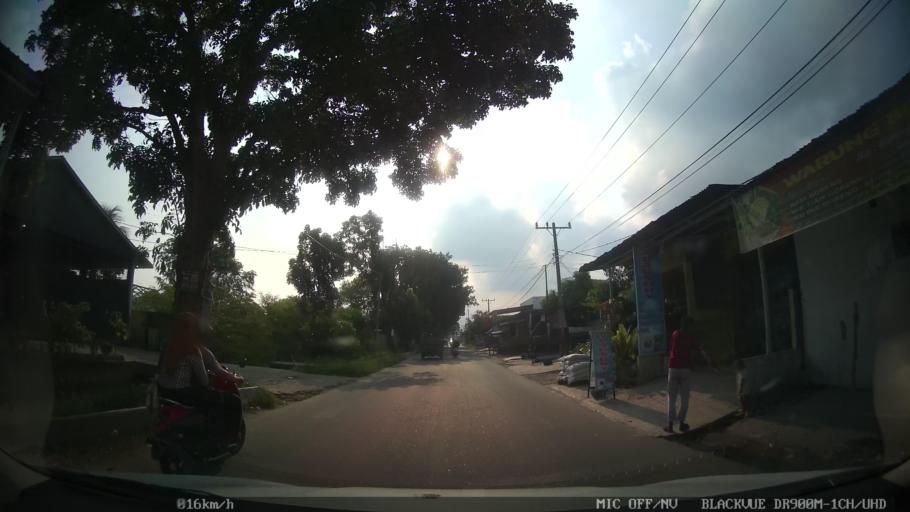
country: ID
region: North Sumatra
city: Medan
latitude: 3.5813
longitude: 98.7493
